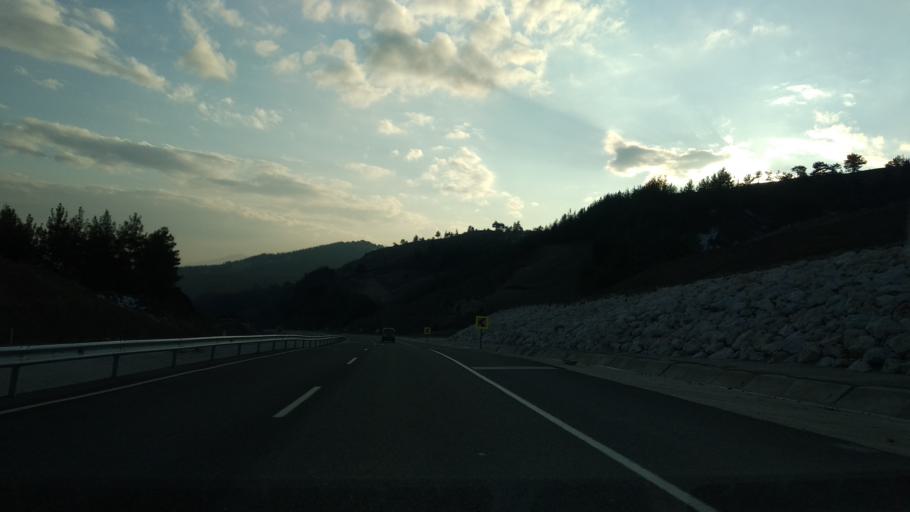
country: TR
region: Kahramanmaras
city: Yenicekale
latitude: 37.7088
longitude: 36.6905
